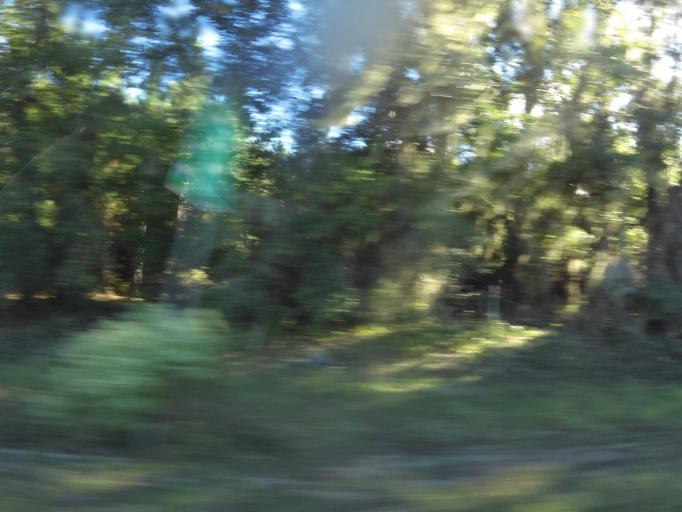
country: US
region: Florida
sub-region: Alachua County
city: Hawthorne
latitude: 29.5277
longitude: -82.1902
